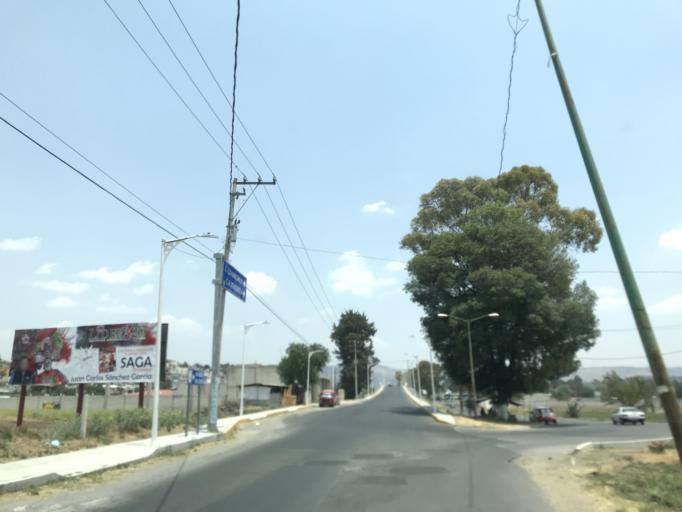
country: MX
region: Tlaxcala
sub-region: Ixtacuixtla de Mariano Matamoros
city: Villa Mariano Matamoros
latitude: 19.3180
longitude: -98.3735
